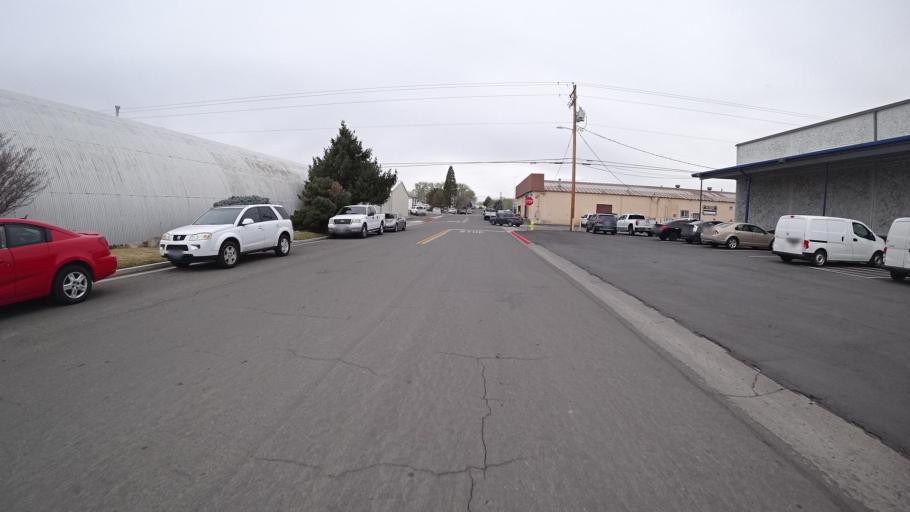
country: US
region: Nevada
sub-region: Washoe County
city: Sparks
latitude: 39.5319
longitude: -119.7671
